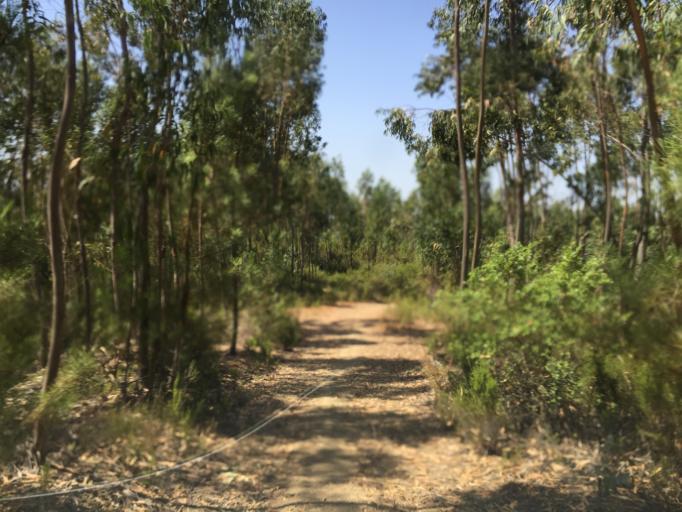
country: PT
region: Santarem
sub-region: Ferreira do Zezere
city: Ferreira do Zezere
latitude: 39.6530
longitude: -8.3144
